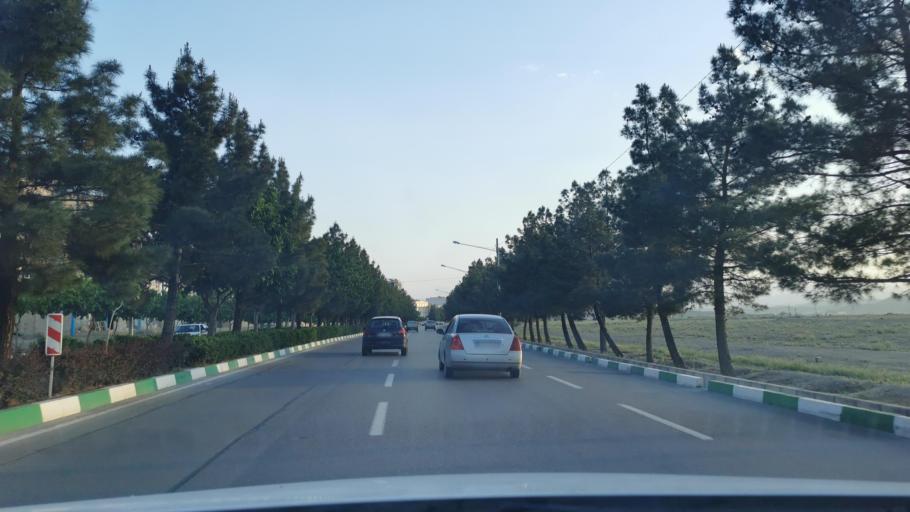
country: IR
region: Razavi Khorasan
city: Torqabeh
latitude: 36.3832
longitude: 59.4630
